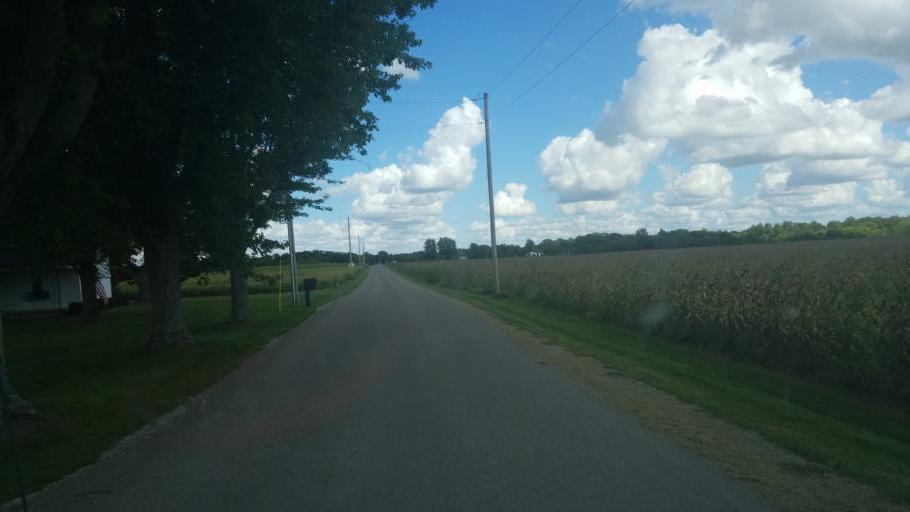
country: US
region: Ohio
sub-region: Hardin County
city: Kenton
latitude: 40.5485
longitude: -83.5444
